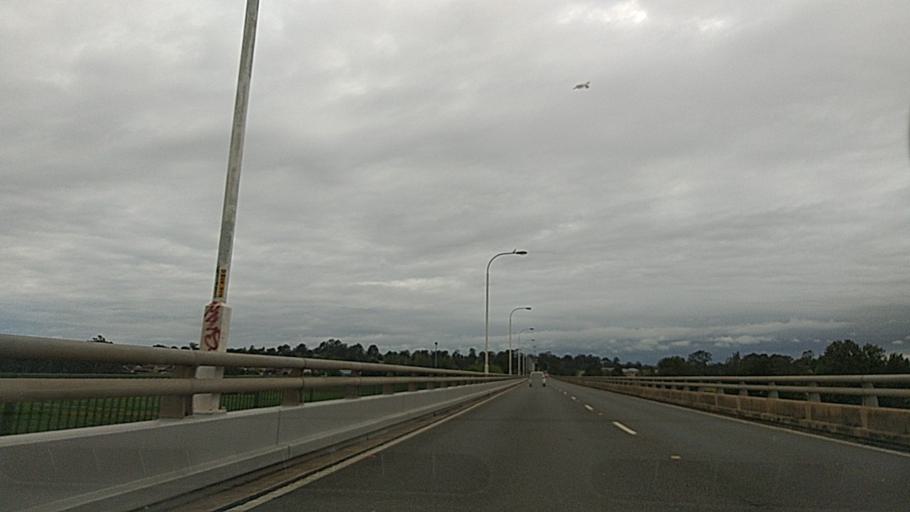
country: AU
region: New South Wales
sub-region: Camden
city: Camden South
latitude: -34.0699
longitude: 150.7030
